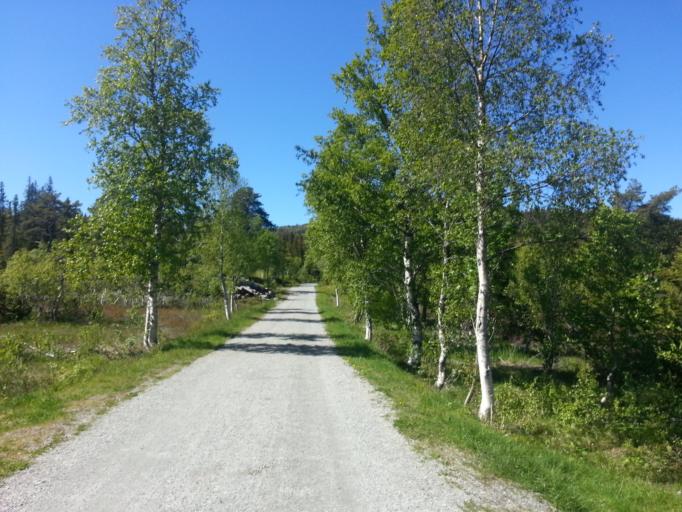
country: NO
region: Sor-Trondelag
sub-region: Trondheim
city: Trondheim
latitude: 63.4124
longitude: 10.2801
